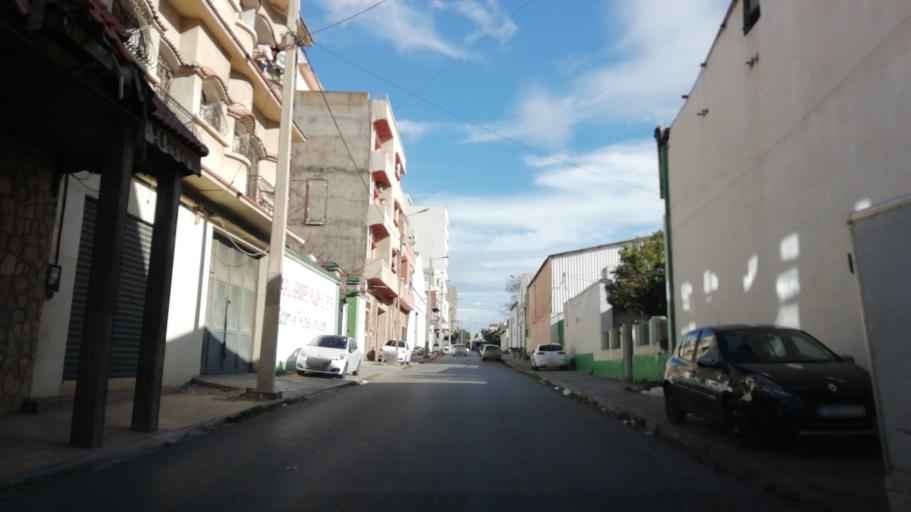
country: DZ
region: Oran
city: Oran
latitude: 35.7003
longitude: -0.6200
